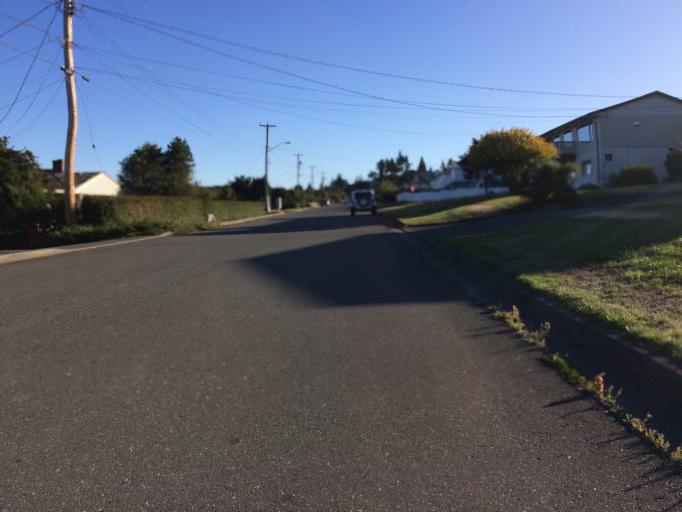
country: CA
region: British Columbia
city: Campbell River
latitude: 50.0064
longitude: -125.2369
